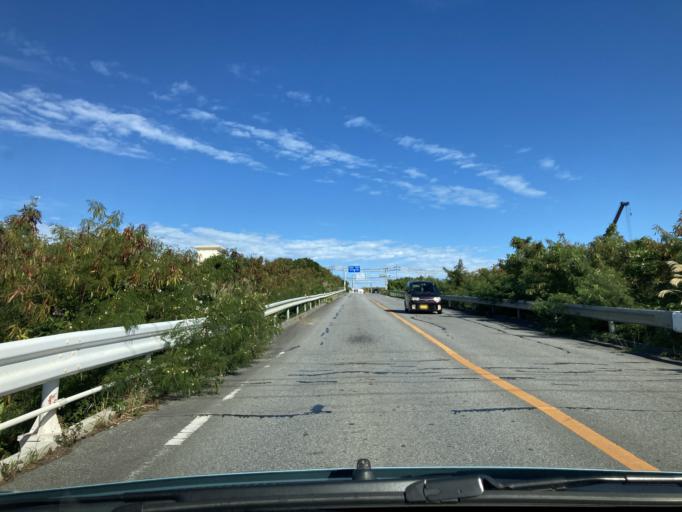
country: JP
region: Okinawa
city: Okinawa
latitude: 26.3806
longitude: 127.7455
